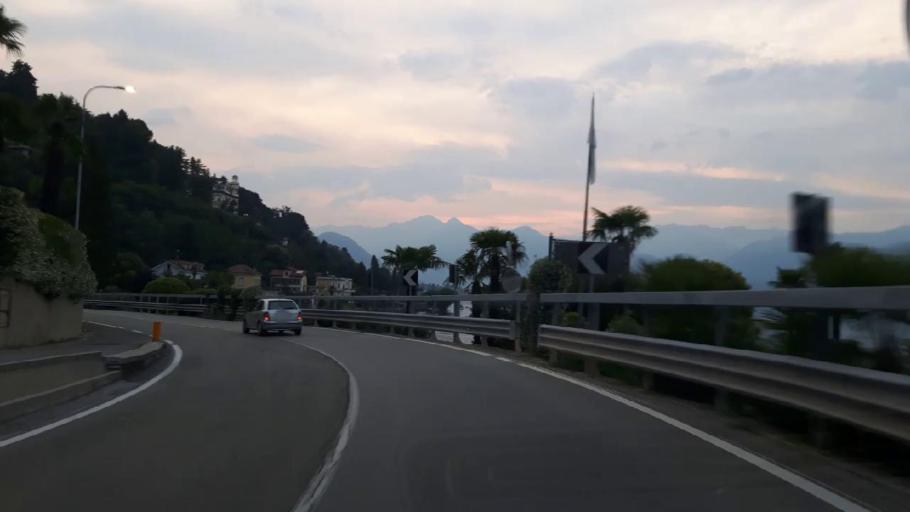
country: IT
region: Piedmont
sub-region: Provincia Verbano-Cusio-Ossola
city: Stresa
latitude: 45.8927
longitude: 8.5181
